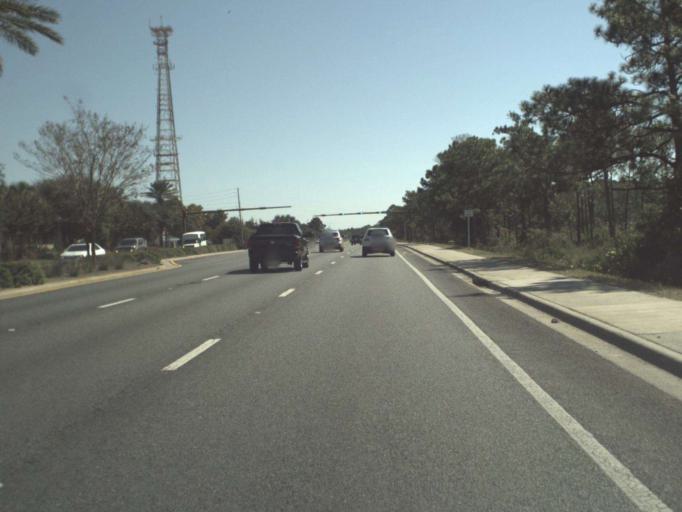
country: US
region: Florida
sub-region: Walton County
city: Miramar Beach
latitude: 30.3776
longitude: -86.3119
